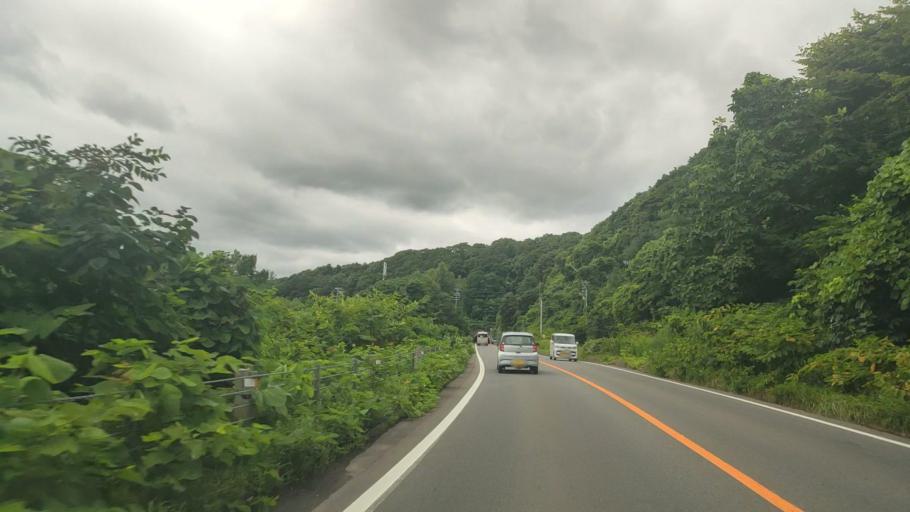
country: JP
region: Hokkaido
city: Date
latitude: 42.5680
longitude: 140.7360
